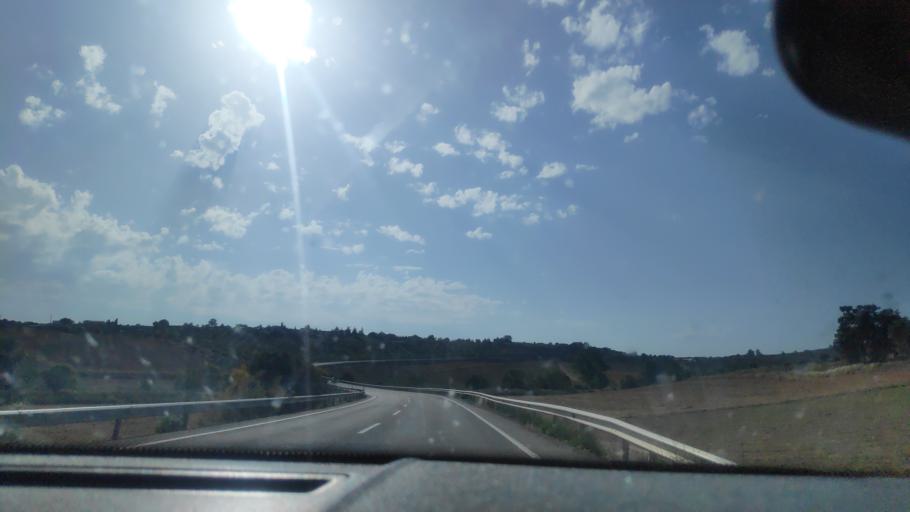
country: ES
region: Andalusia
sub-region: Provincia de Jaen
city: Frailes
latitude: 37.4453
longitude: -3.8616
